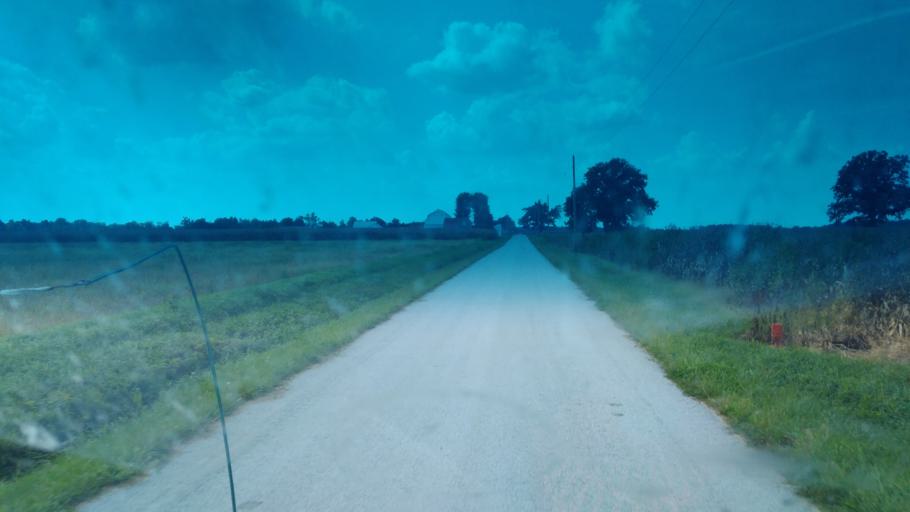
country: US
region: Ohio
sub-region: Hardin County
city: Kenton
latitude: 40.6893
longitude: -83.7162
